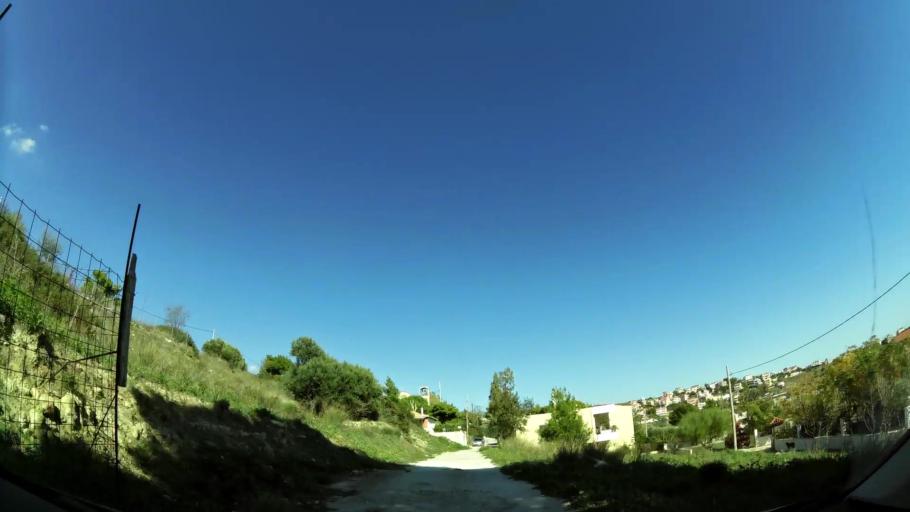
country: GR
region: Attica
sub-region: Nomarchia Anatolikis Attikis
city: Dhrafi
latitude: 38.0055
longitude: 23.9064
